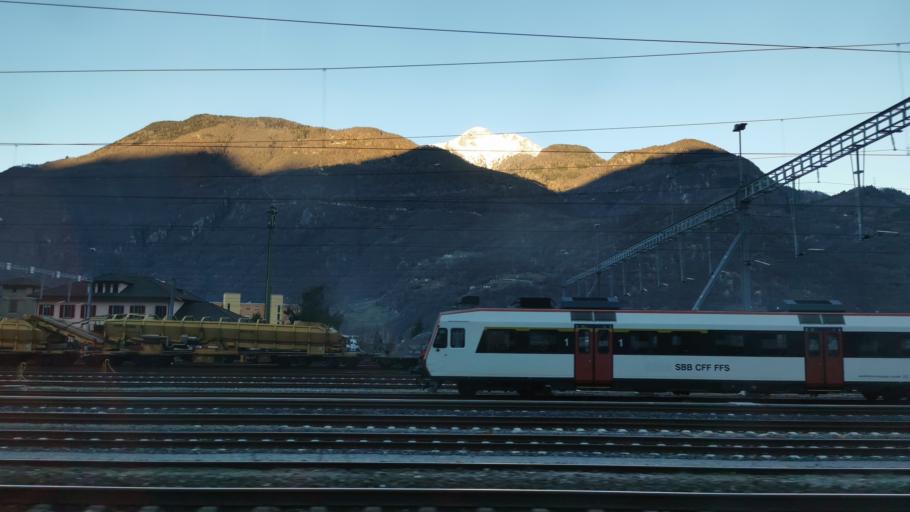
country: CH
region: Ticino
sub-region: Bellinzona District
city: Bellinzona
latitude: 46.2035
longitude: 9.0384
